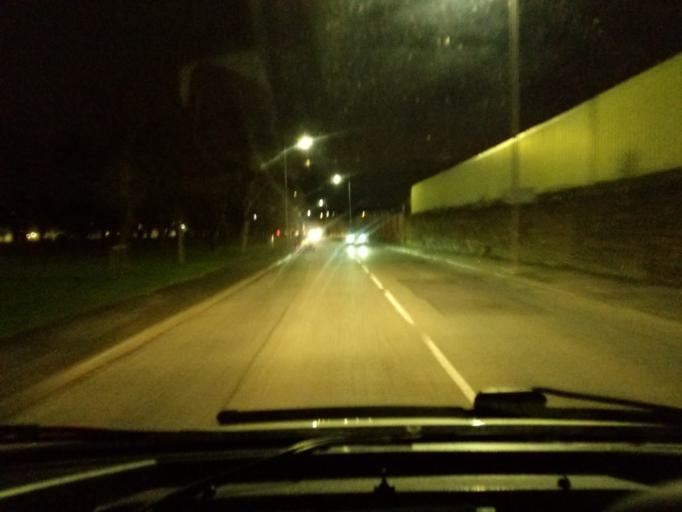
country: GB
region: England
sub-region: St. Helens
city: St Helens
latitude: 53.4638
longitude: -2.7417
